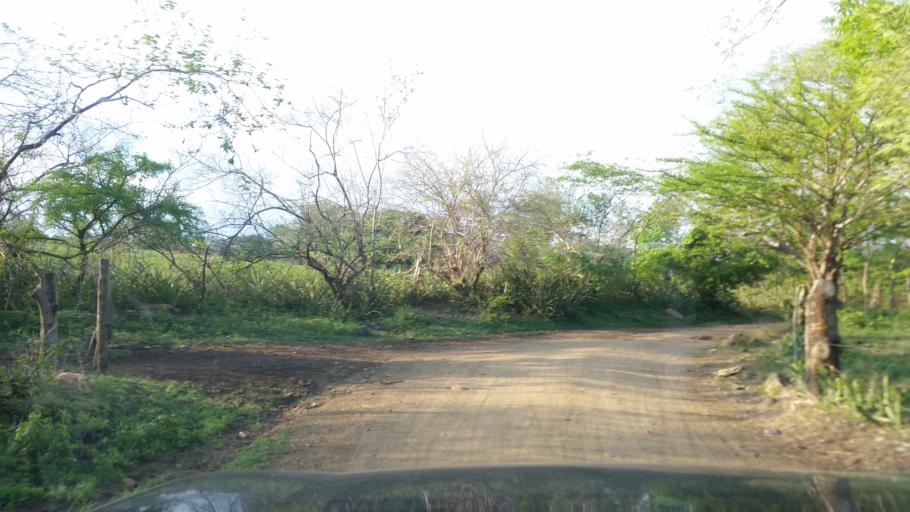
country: NI
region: Managua
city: Masachapa
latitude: 11.7837
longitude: -86.4733
